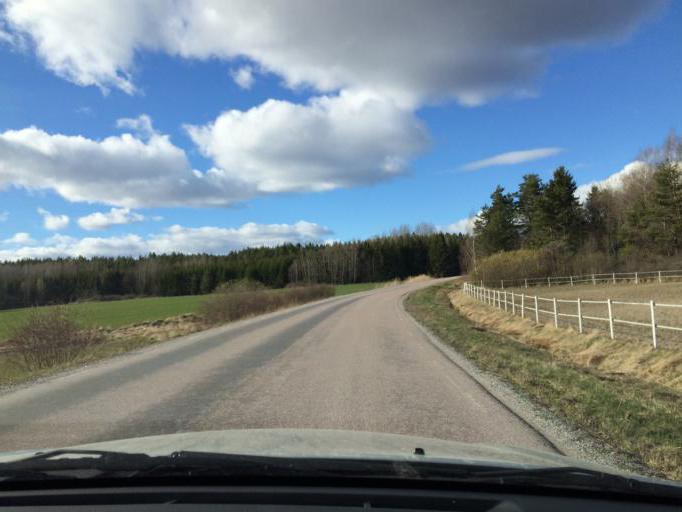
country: SE
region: Soedermanland
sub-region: Eskilstuna Kommun
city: Hallbybrunn
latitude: 59.4179
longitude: 16.4366
